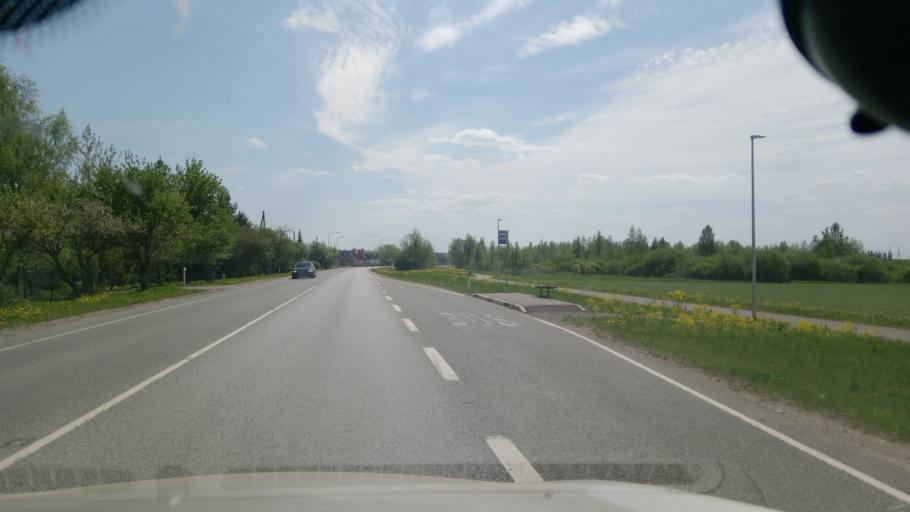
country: EE
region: Laeaene-Virumaa
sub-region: Rakvere linn
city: Rakvere
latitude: 59.3694
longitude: 26.3357
